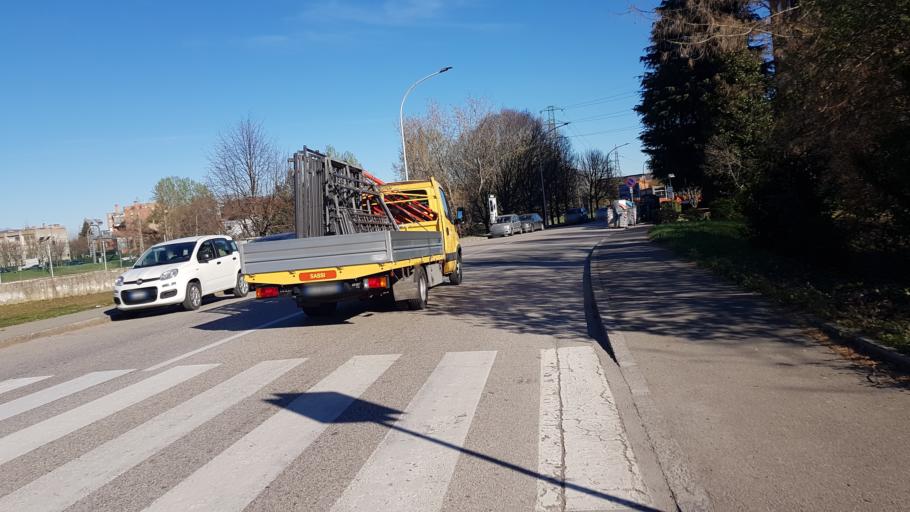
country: IT
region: Emilia-Romagna
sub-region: Provincia di Bologna
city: Bologna
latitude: 44.5220
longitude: 11.3272
